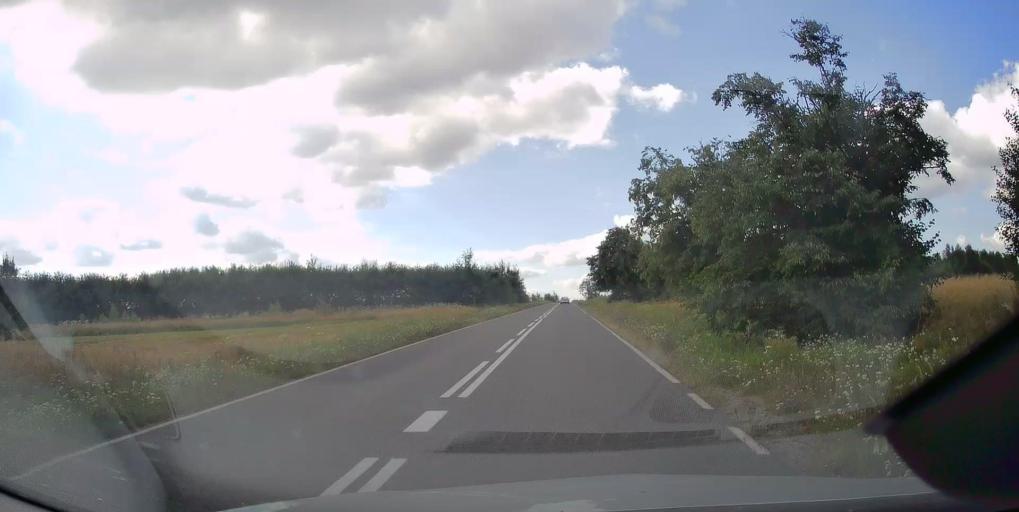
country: PL
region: Swietokrzyskie
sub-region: Powiat kielecki
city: Bodzentyn
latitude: 50.9028
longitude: 21.0142
